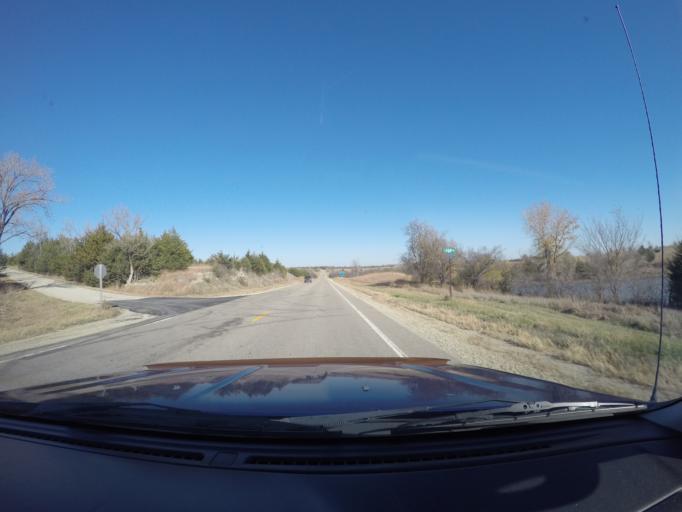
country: US
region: Kansas
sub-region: Riley County
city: Manhattan
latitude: 39.3777
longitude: -96.7565
